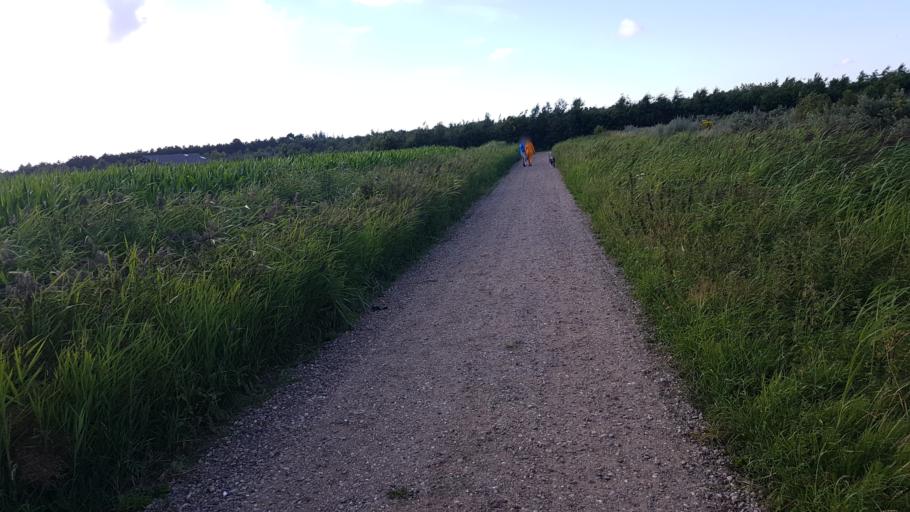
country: DE
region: Schleswig-Holstein
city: List
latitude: 55.0914
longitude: 8.5374
